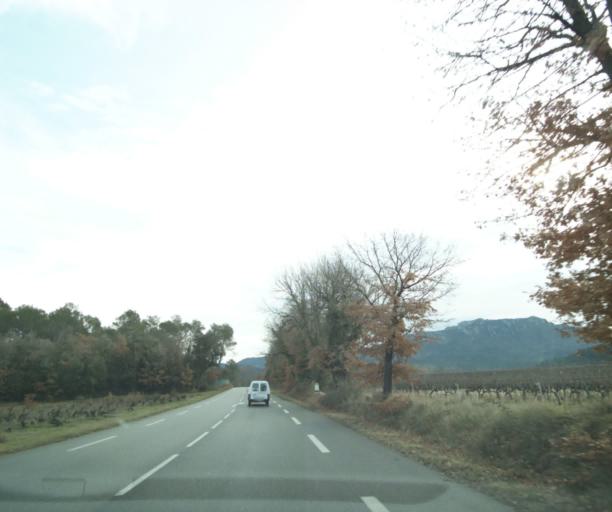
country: FR
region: Provence-Alpes-Cote d'Azur
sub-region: Departement du Var
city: Tourves
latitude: 43.3966
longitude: 5.9696
